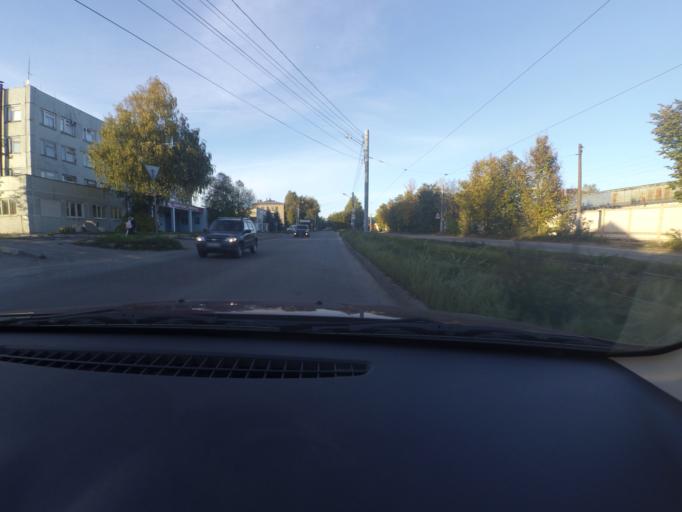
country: RU
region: Nizjnij Novgorod
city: Nizhniy Novgorod
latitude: 56.2835
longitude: 43.9935
